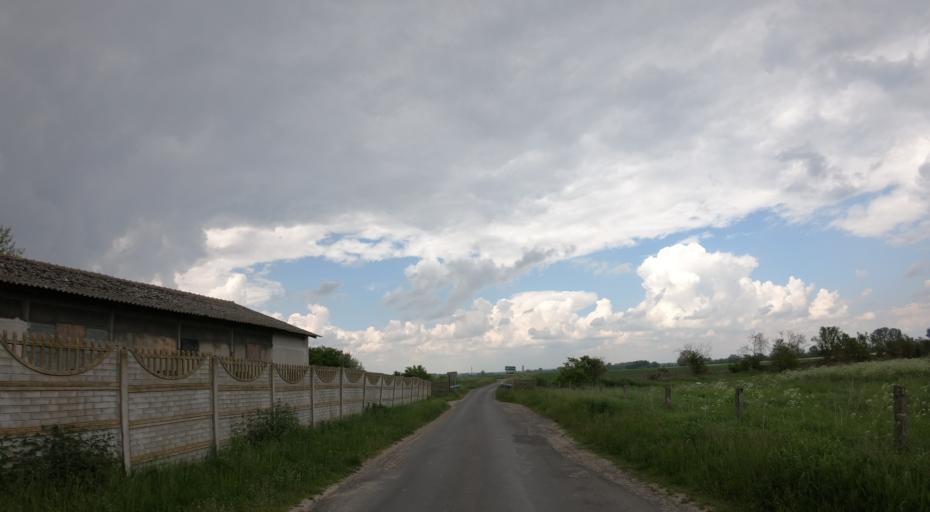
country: PL
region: West Pomeranian Voivodeship
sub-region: Powiat pyrzycki
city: Bielice
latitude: 53.2050
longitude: 14.7691
